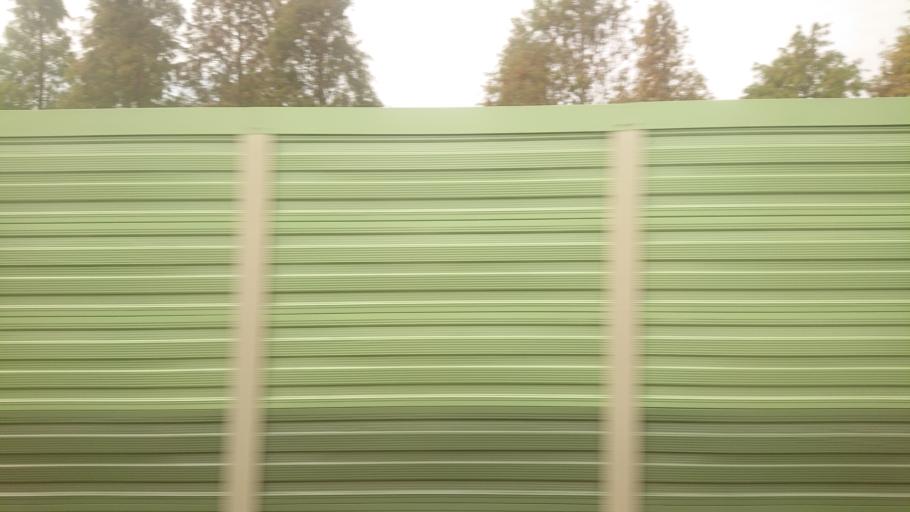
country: TW
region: Taiwan
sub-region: Changhua
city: Chang-hua
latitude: 24.0280
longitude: 120.5358
